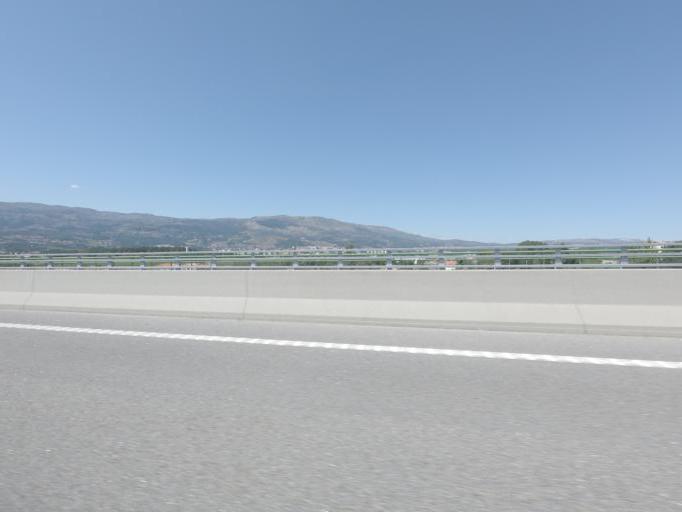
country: PT
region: Vila Real
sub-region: Vila Real
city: Vila Real
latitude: 41.2773
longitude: -7.7348
